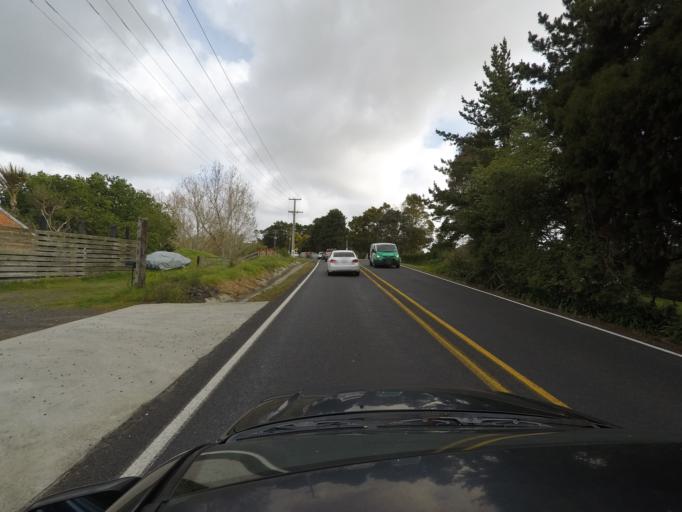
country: NZ
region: Auckland
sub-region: Auckland
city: Pakuranga
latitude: -36.9402
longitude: 174.9459
